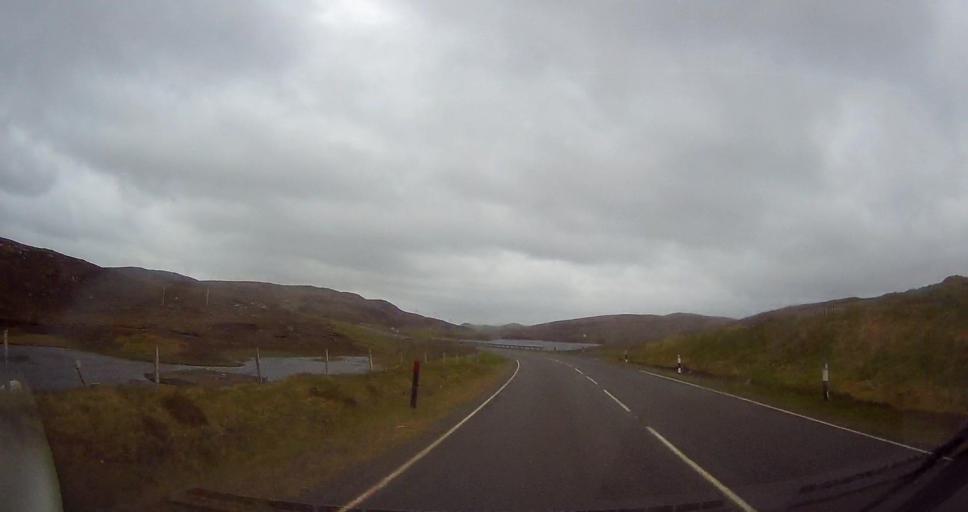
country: GB
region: Scotland
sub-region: Shetland Islands
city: Lerwick
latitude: 60.4477
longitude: -1.3958
